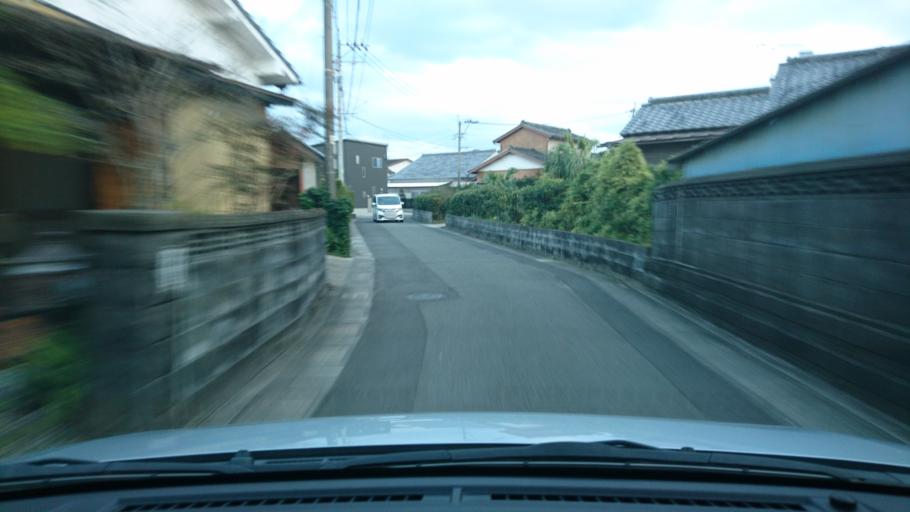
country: JP
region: Miyazaki
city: Miyazaki-shi
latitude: 31.8520
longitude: 131.4318
